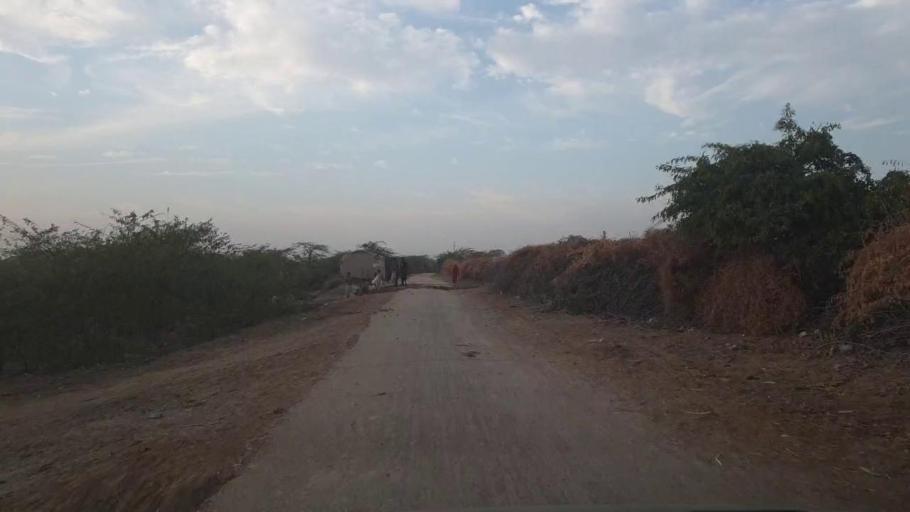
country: PK
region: Sindh
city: Umarkot
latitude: 25.2791
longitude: 69.6841
